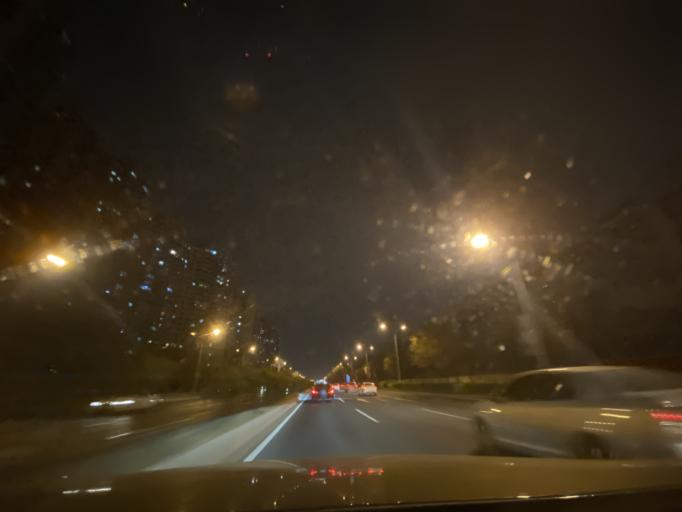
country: CN
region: Beijing
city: Lugouqiao
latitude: 39.8958
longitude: 116.3008
